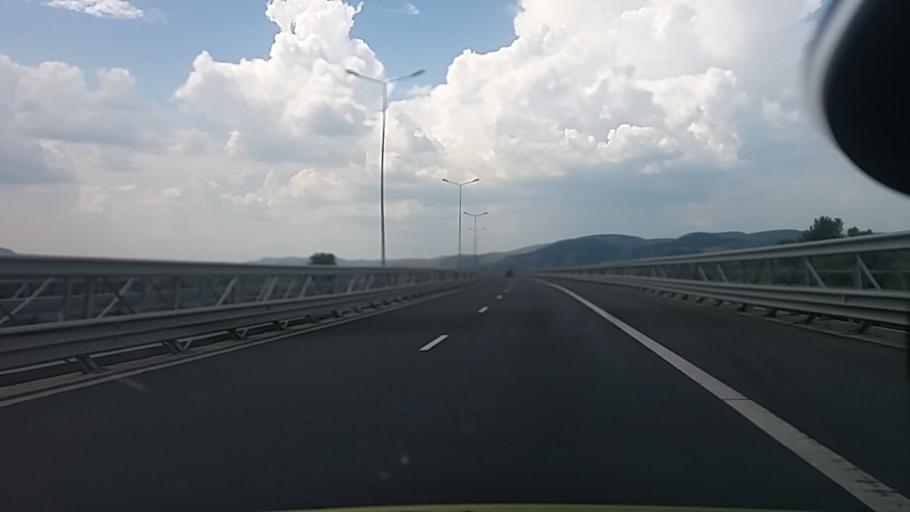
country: RO
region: Hunedoara
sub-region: Oras Simeria
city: Simeria
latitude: 45.8661
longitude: 23.0237
